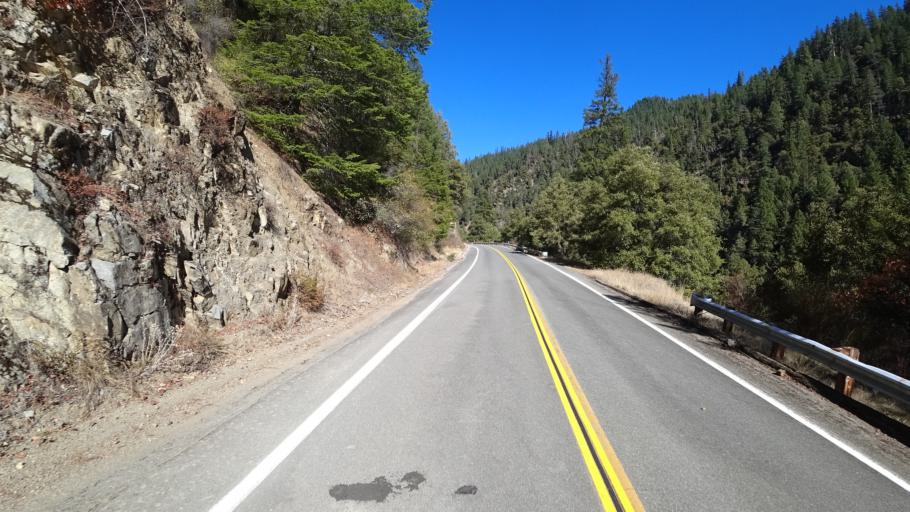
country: US
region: California
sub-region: Siskiyou County
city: Happy Camp
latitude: 41.3530
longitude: -123.4094
